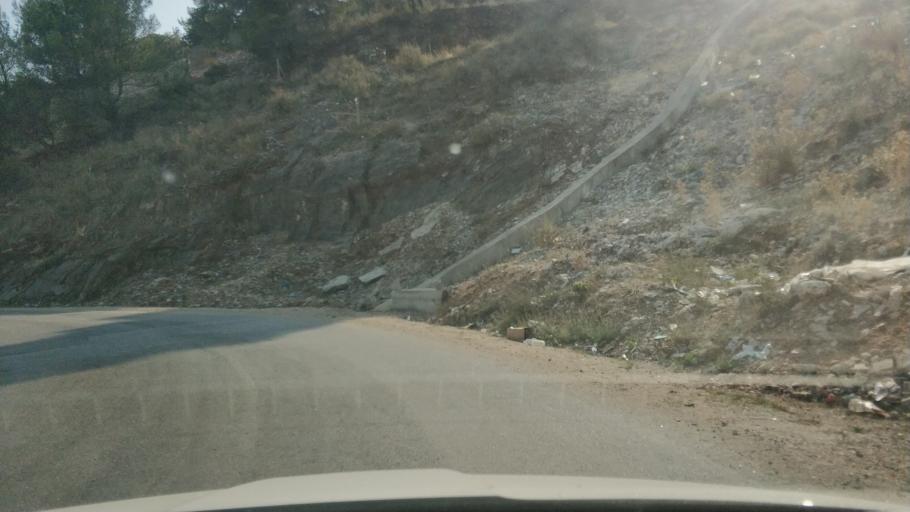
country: AL
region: Vlore
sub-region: Rrethi i Sarandes
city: Sarande
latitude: 39.8703
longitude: 20.0303
